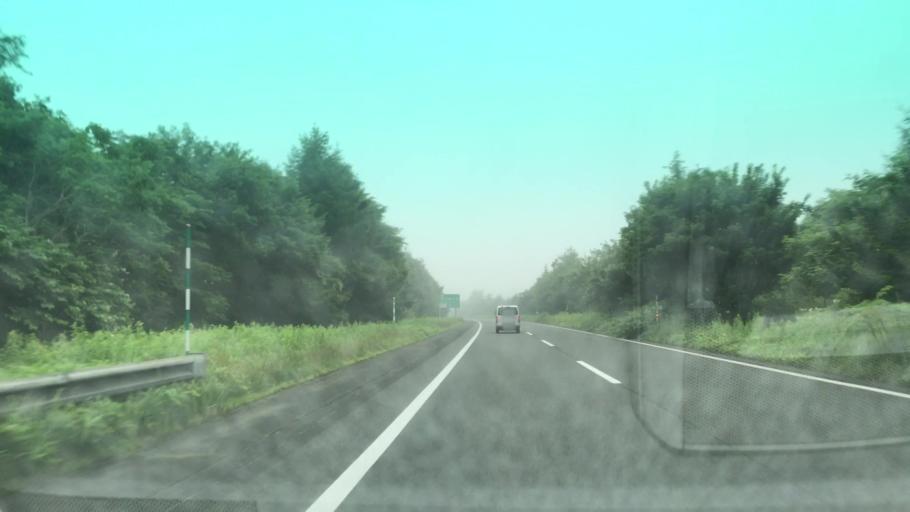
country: JP
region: Hokkaido
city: Chitose
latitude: 42.7887
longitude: 141.6266
